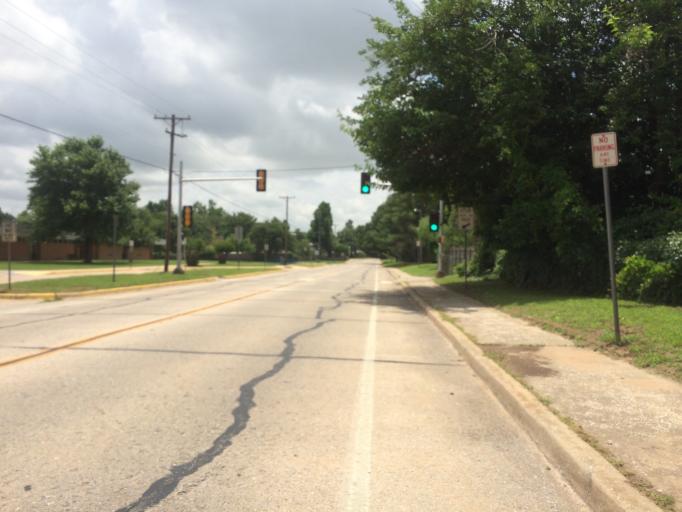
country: US
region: Oklahoma
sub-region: Cleveland County
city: Norman
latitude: 35.1989
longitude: -97.4679
